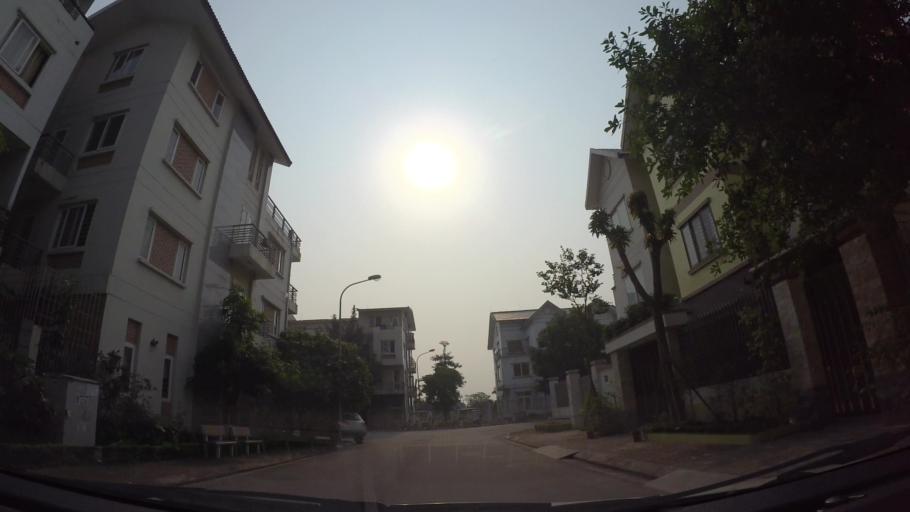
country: VN
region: Ha Noi
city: Ha Dong
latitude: 20.9969
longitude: 105.7452
